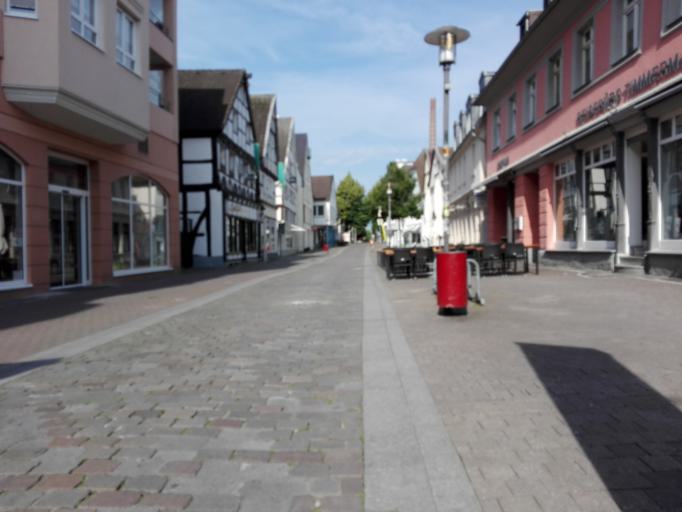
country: DE
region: North Rhine-Westphalia
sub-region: Regierungsbezirk Arnsberg
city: Unna
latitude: 51.5345
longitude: 7.6878
